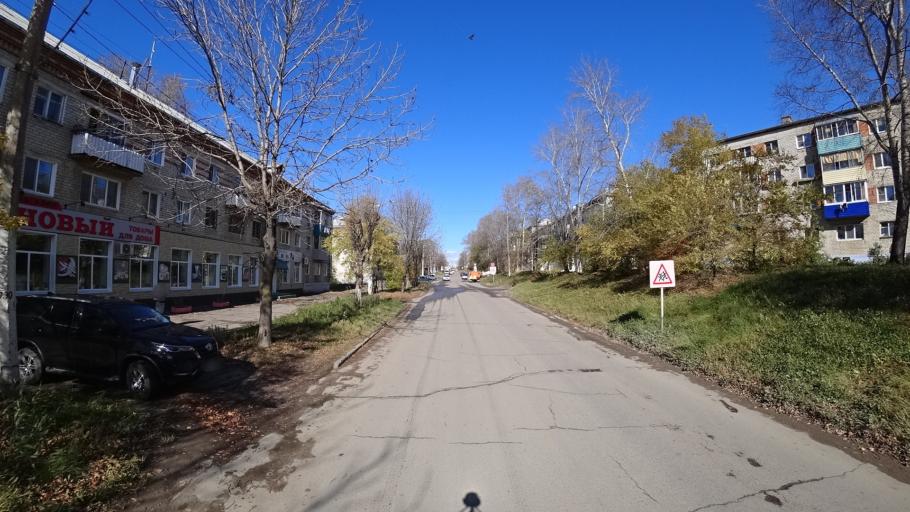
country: RU
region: Khabarovsk Krai
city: Amursk
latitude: 50.2176
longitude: 136.9032
